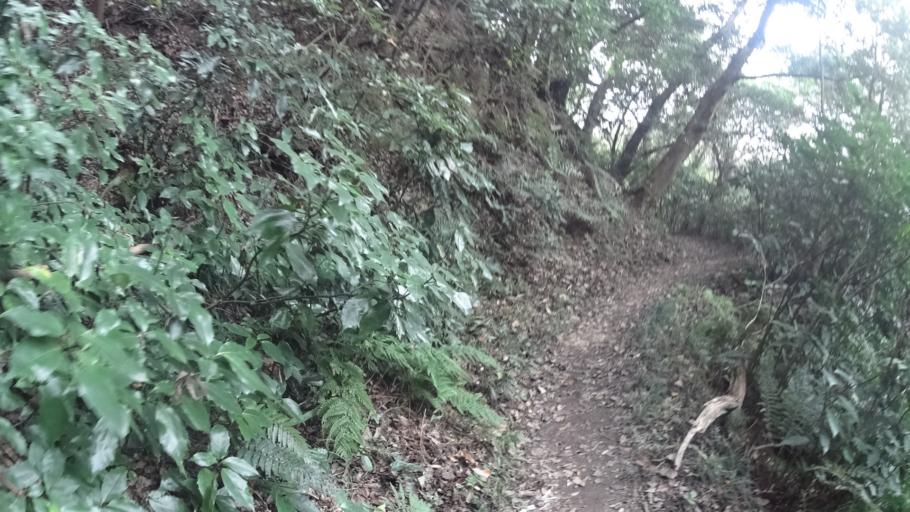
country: JP
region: Kanagawa
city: Zushi
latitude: 35.2909
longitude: 139.6092
